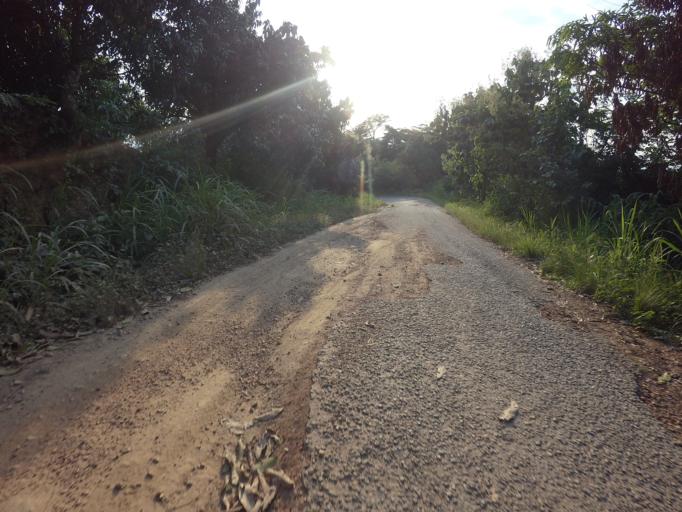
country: TG
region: Plateaux
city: Kpalime
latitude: 6.8885
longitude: 0.4477
